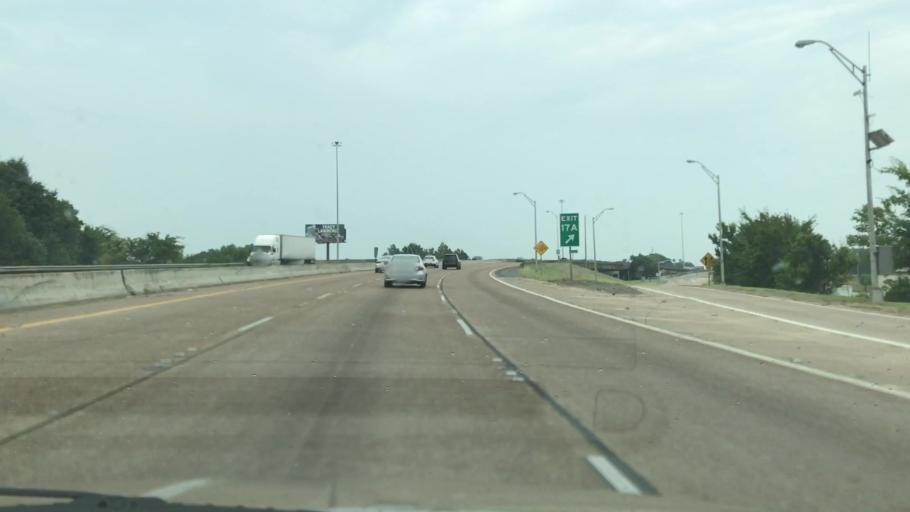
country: US
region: Louisiana
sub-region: Caddo Parish
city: Shreveport
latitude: 32.4901
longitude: -93.7721
